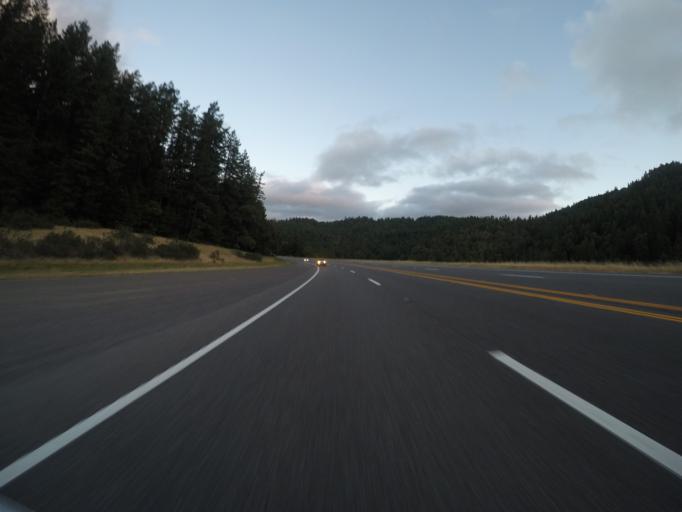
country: US
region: California
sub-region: Humboldt County
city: Redway
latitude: 40.0518
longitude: -123.7925
